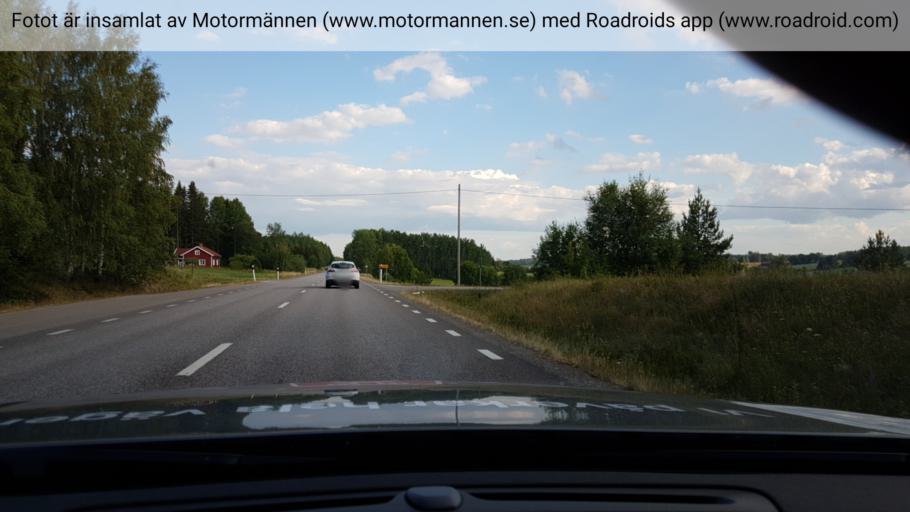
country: SE
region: Uppsala
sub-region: Heby Kommun
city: Heby
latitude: 59.9118
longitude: 16.8897
